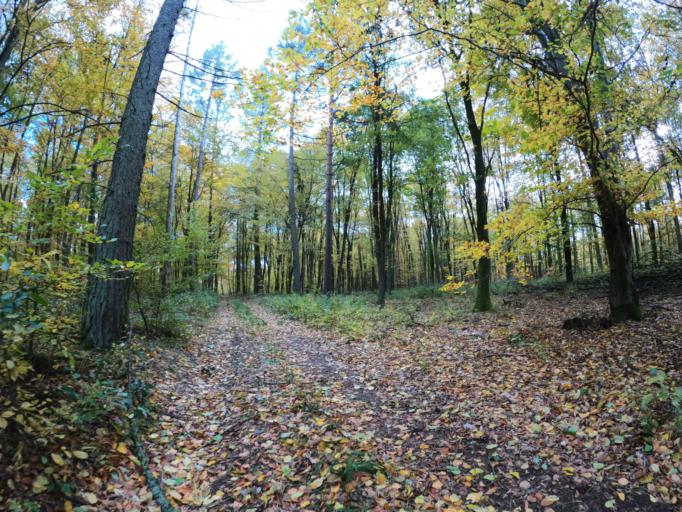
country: PL
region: West Pomeranian Voivodeship
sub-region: Powiat mysliborski
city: Barlinek
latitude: 52.9610
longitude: 15.2656
